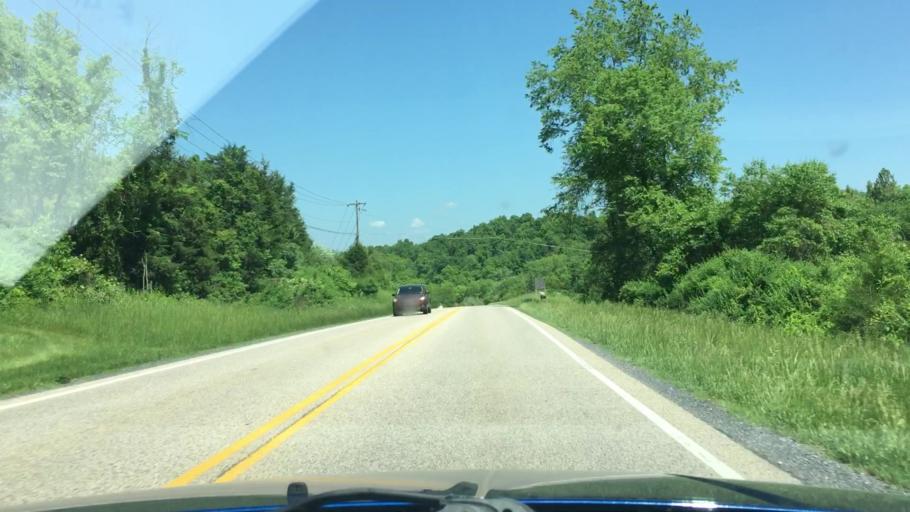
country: US
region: Virginia
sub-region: City of Staunton
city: Staunton
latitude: 38.1860
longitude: -79.1015
